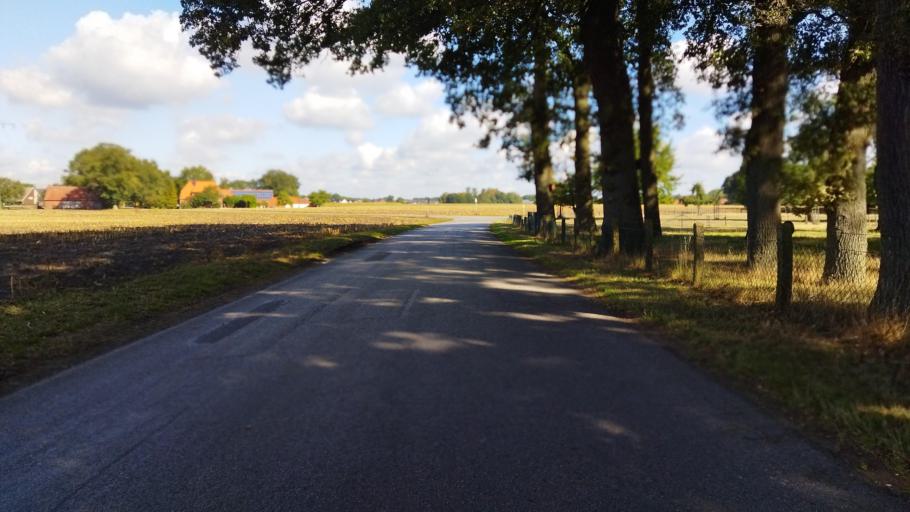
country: DE
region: Lower Saxony
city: Salzbergen
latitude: 52.3094
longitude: 7.3245
